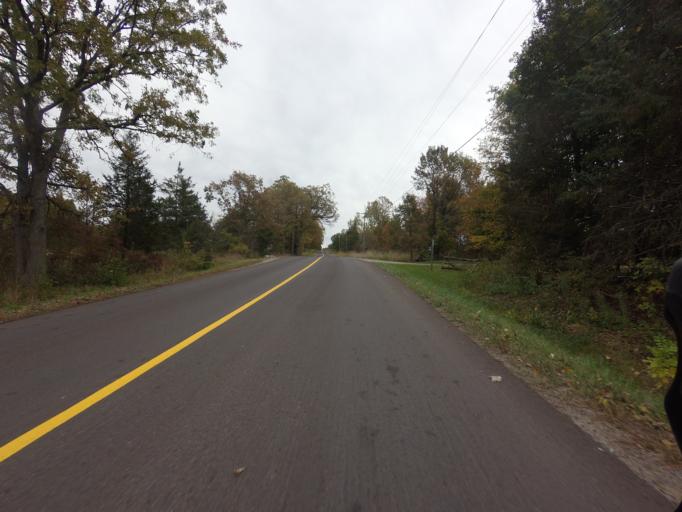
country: CA
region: Ontario
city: Gananoque
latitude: 44.5814
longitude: -76.0620
